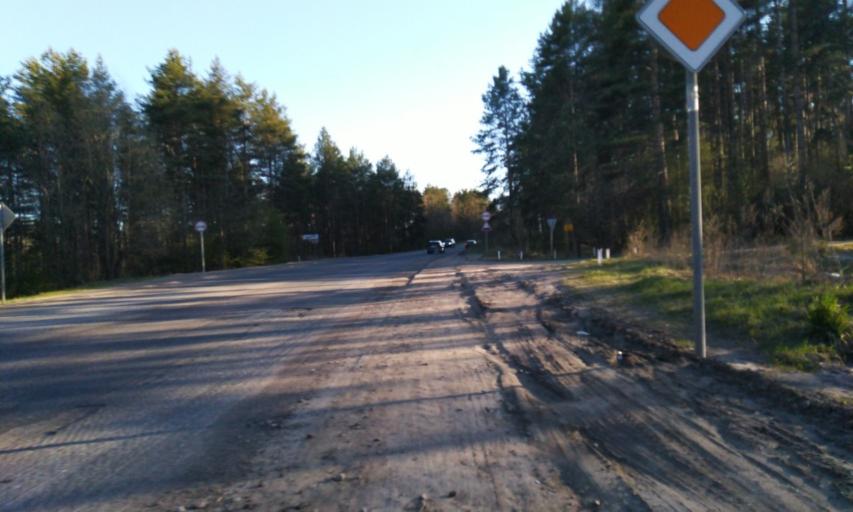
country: RU
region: Leningrad
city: Toksovo
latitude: 60.1336
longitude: 30.5265
